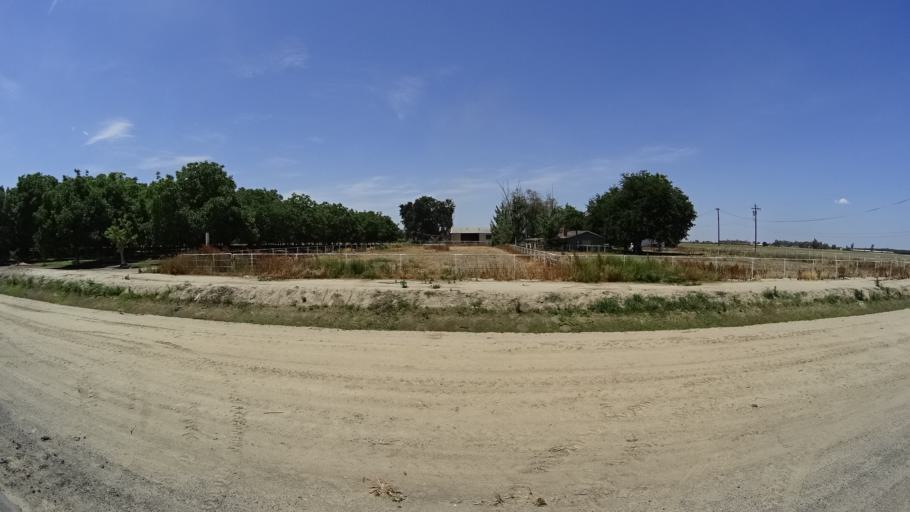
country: US
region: California
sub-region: Kings County
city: Home Garden
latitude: 36.2760
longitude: -119.6727
